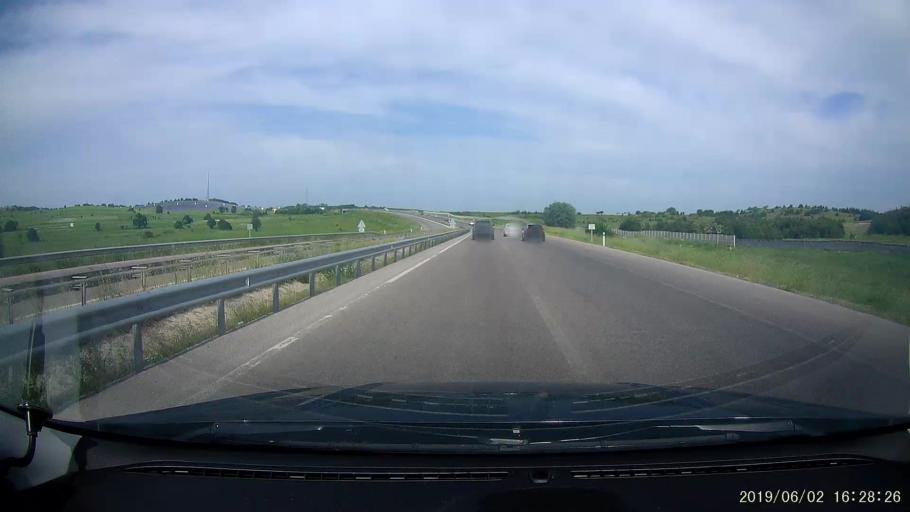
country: TR
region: Samsun
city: Ladik
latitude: 41.0068
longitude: 35.8478
